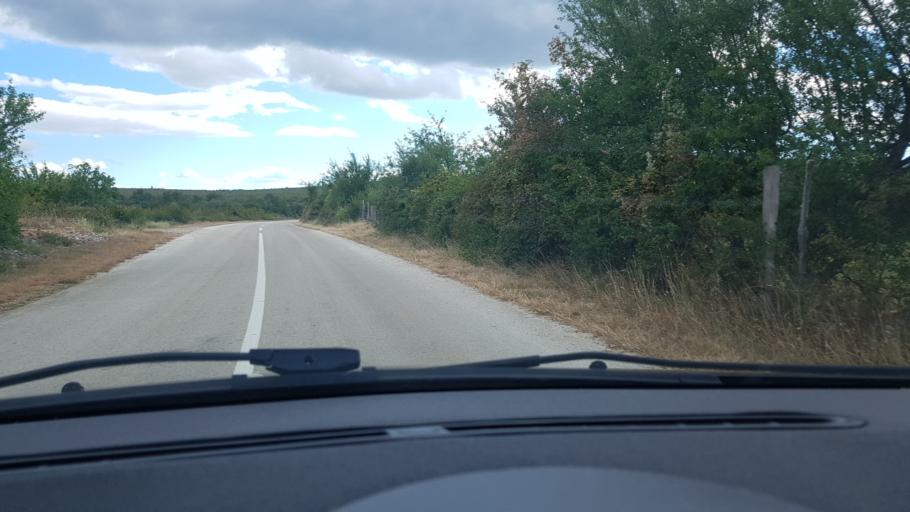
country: HR
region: Sibensko-Kniniska
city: Kistanje
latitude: 44.1032
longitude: 15.9405
